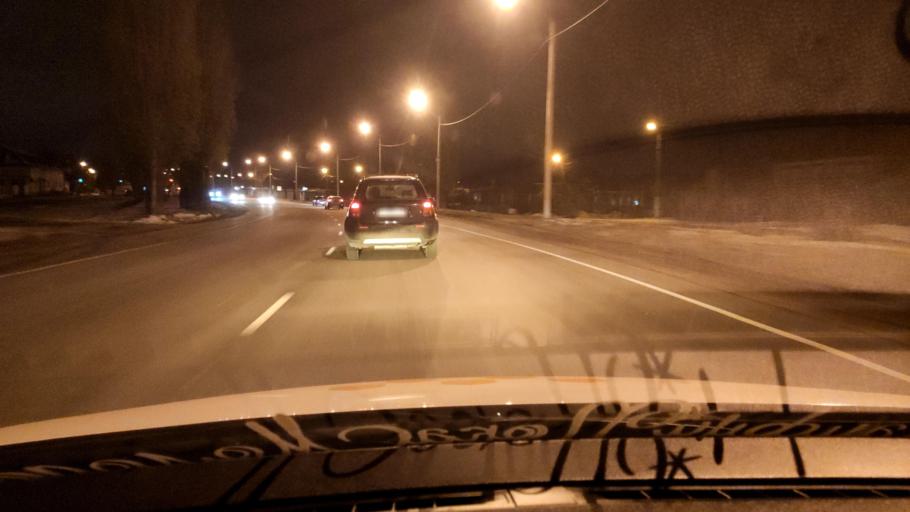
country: RU
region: Voronezj
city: Pridonskoy
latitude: 51.7095
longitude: 39.0737
